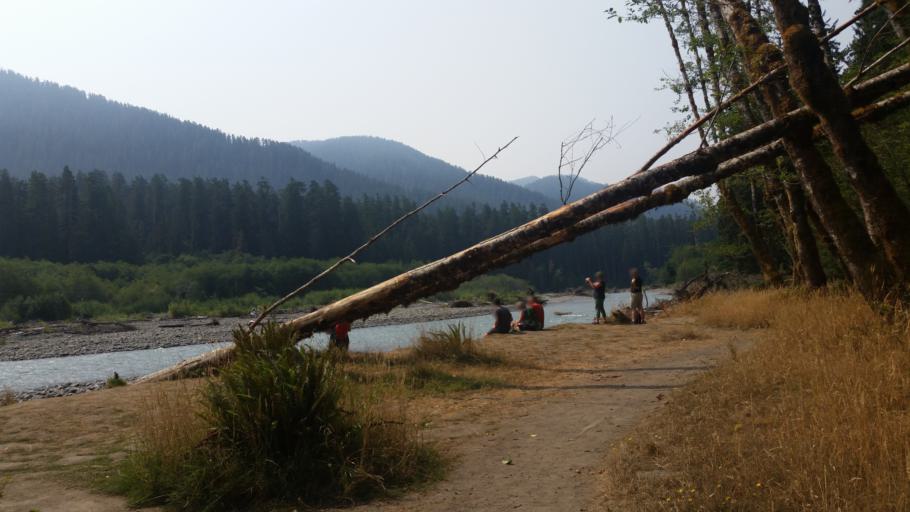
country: US
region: Washington
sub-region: Clallam County
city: Forks
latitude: 47.8595
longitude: -123.9261
